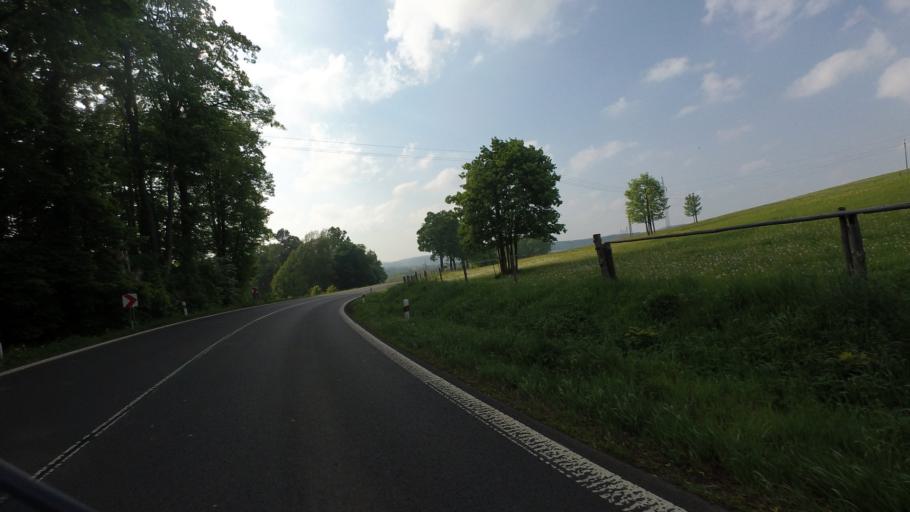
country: CZ
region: Ustecky
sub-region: Okres Decin
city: Sluknov
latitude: 50.9906
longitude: 14.4851
